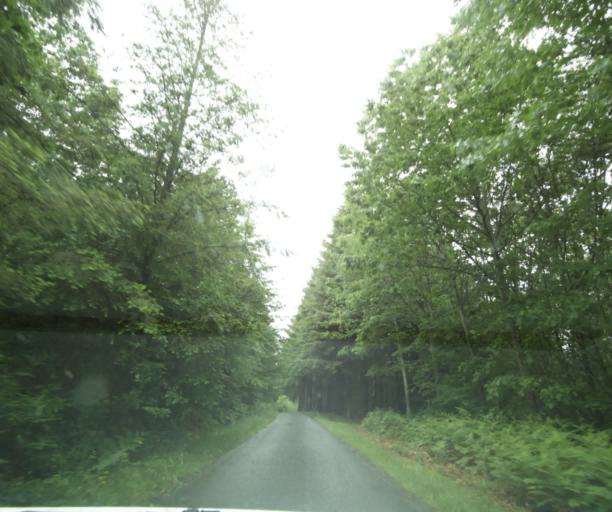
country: FR
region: Bourgogne
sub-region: Departement de Saone-et-Loire
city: Palinges
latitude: 46.5359
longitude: 4.2637
